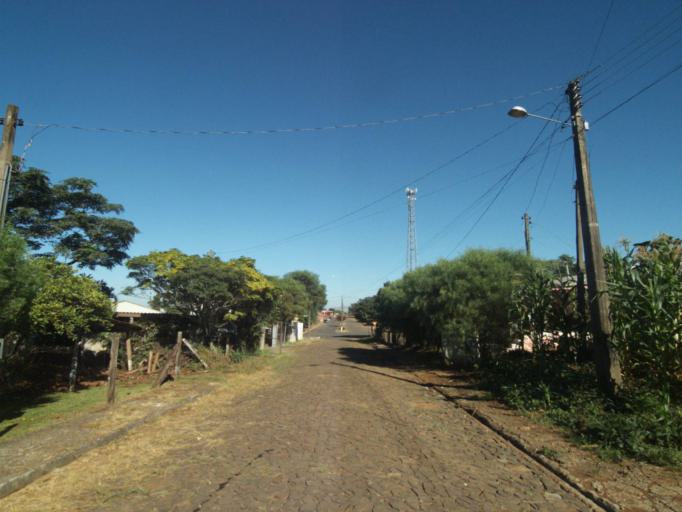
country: BR
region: Parana
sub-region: Pinhao
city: Pinhao
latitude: -25.8352
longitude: -52.0254
